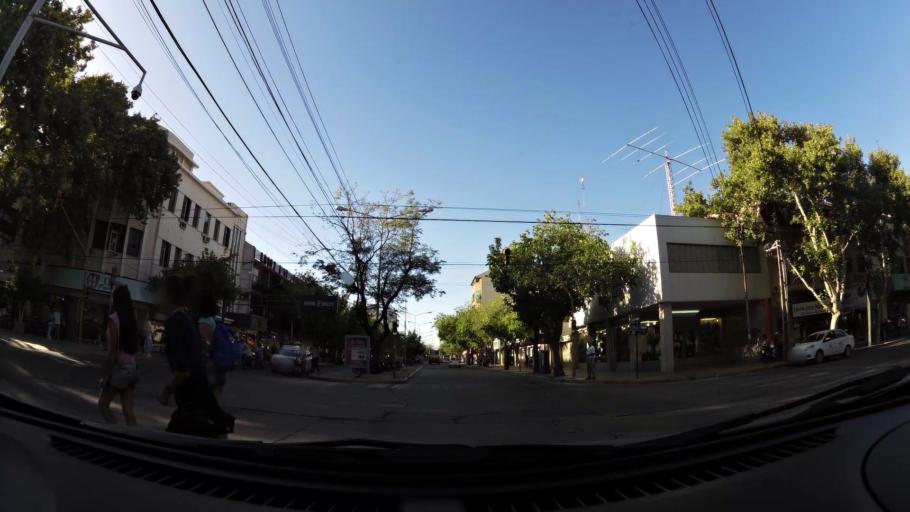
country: AR
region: San Juan
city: San Juan
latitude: -31.5364
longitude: -68.5215
